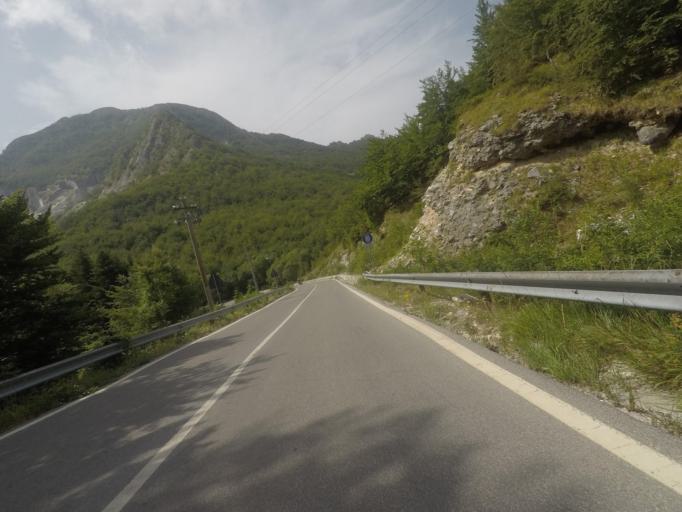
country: IT
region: Tuscany
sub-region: Provincia di Lucca
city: Fontana delle Monache
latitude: 44.0634
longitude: 10.2335
